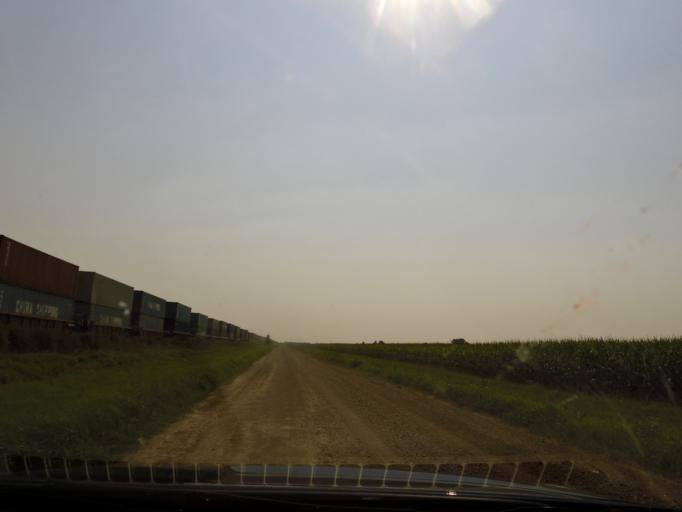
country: US
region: North Dakota
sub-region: Ransom County
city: Sheldon
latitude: 46.2600
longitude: -97.1196
